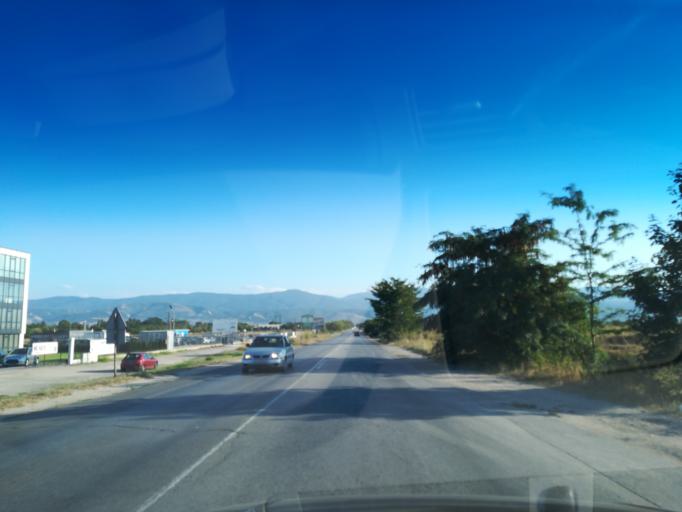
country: BG
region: Plovdiv
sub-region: Obshtina Plovdiv
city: Plovdiv
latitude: 42.1479
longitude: 24.6759
